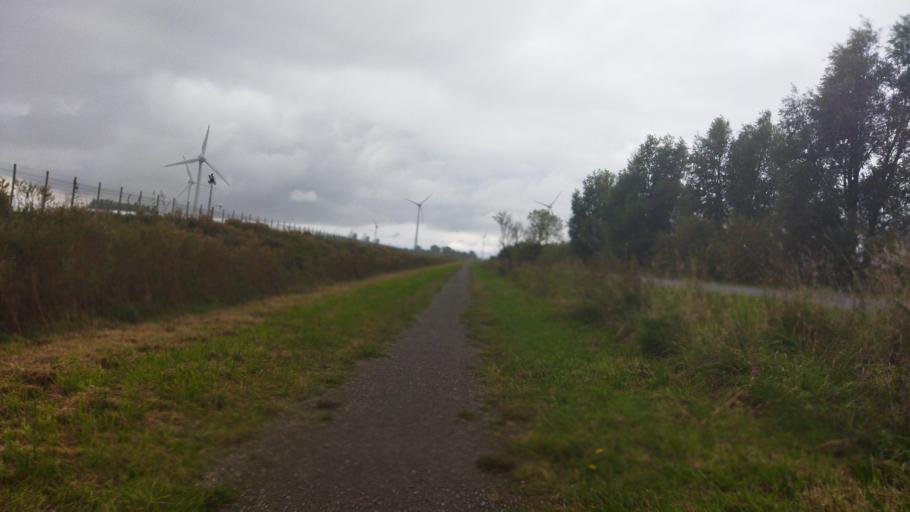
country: DE
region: Lower Saxony
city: Emden
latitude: 53.3509
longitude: 7.1433
